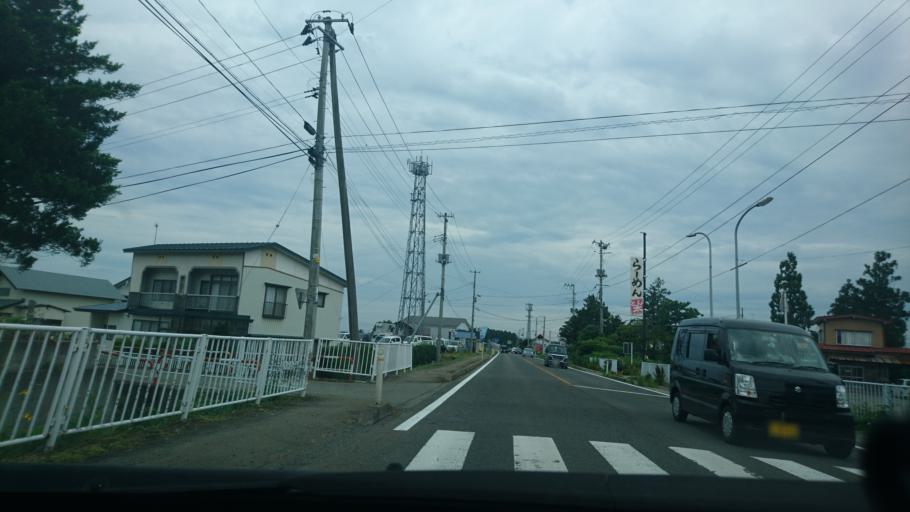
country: JP
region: Akita
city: Omagari
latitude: 39.4102
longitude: 140.5552
